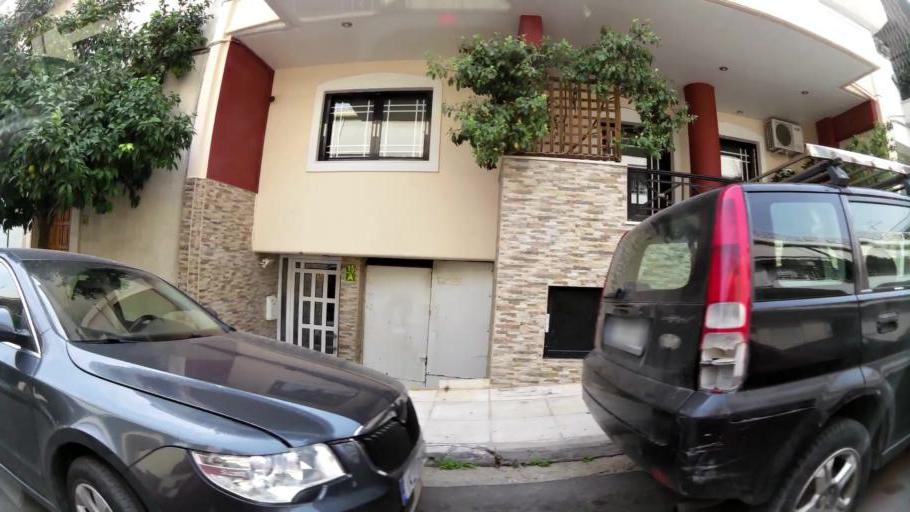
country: GR
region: Attica
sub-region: Nomarchia Athinas
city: Chaidari
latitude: 38.0127
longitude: 23.6783
